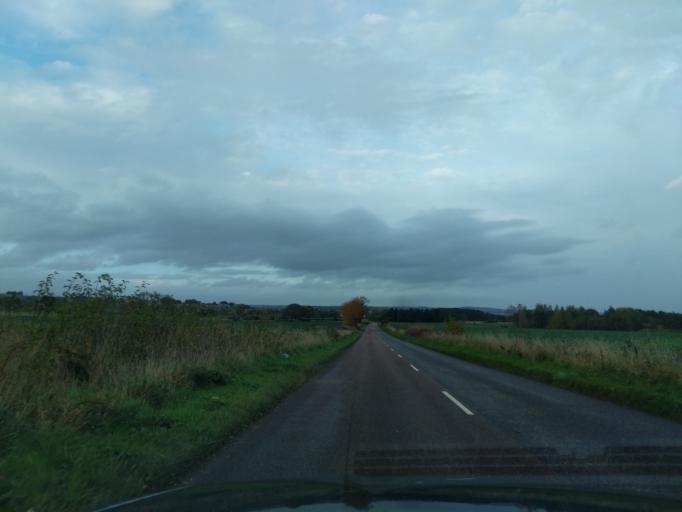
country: GB
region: Scotland
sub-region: Fife
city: Tayport
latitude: 56.4300
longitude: -2.8873
